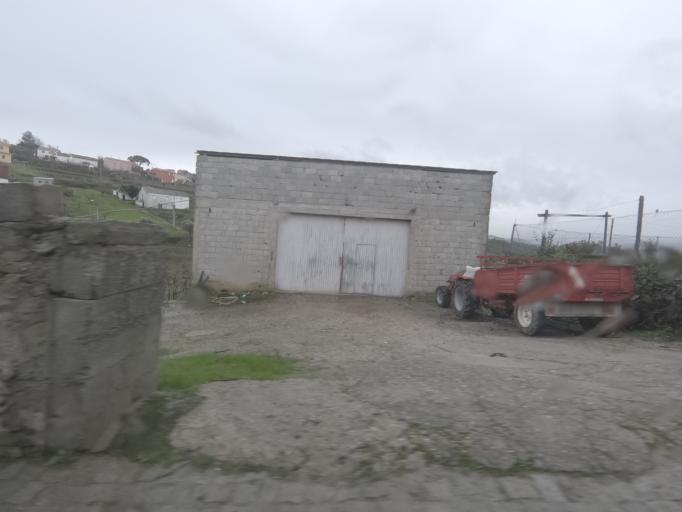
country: PT
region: Vila Real
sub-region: Peso da Regua
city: Peso da Regua
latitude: 41.1756
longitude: -7.7270
